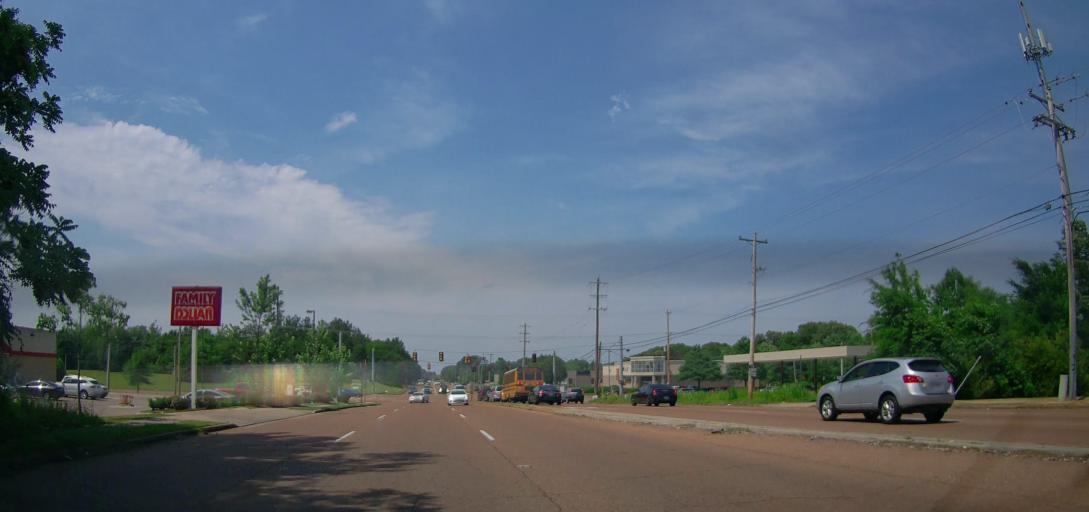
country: US
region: Mississippi
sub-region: De Soto County
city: Olive Branch
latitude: 35.0049
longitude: -89.8310
